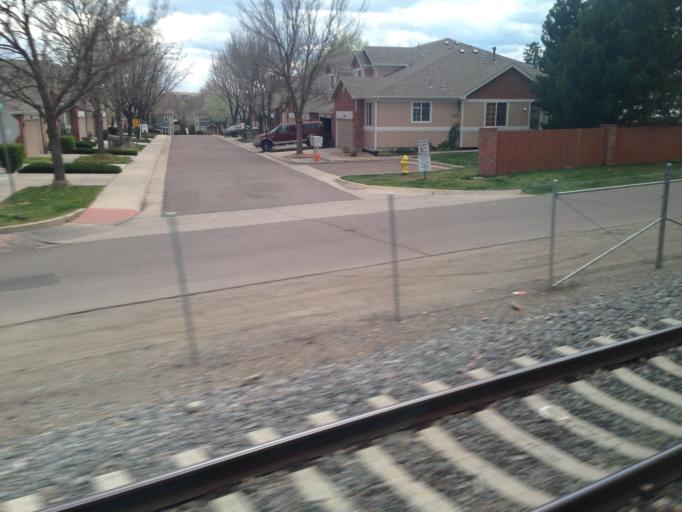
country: US
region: Colorado
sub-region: Jefferson County
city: Arvada
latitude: 39.7966
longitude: -105.0899
